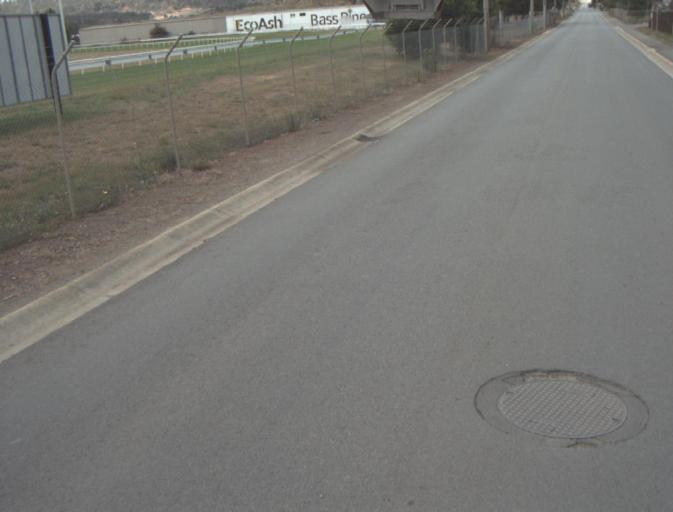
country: AU
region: Tasmania
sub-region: Launceston
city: Newnham
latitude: -41.4061
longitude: 147.1450
